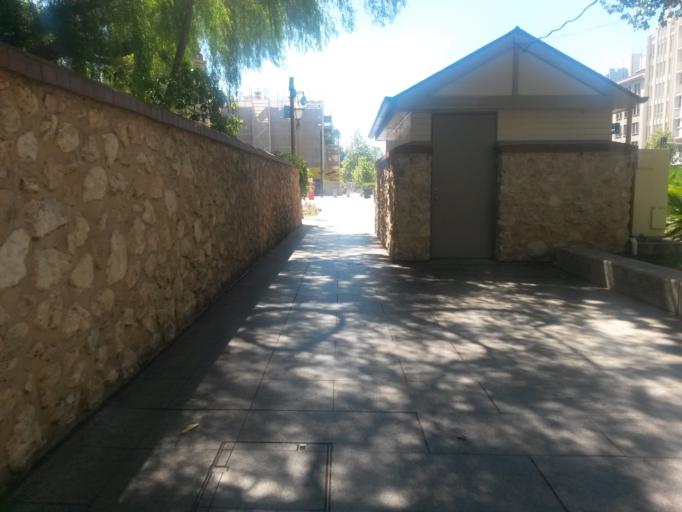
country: AU
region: South Australia
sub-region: Adelaide
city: Adelaide
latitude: -34.9212
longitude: 138.6012
